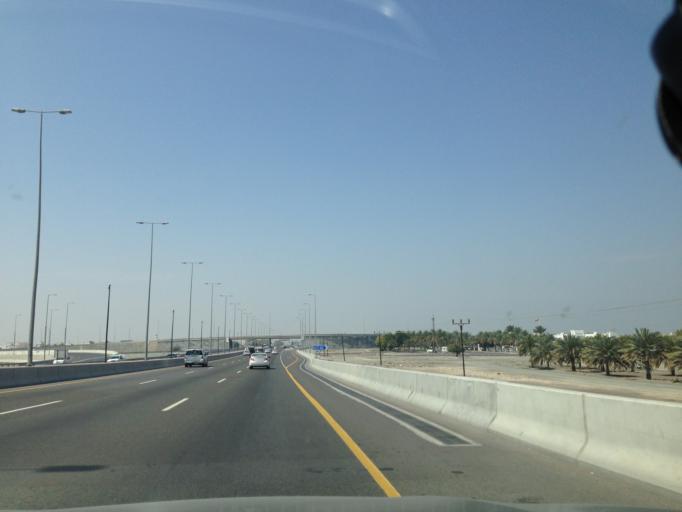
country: OM
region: Muhafazat Masqat
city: As Sib al Jadidah
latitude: 23.6644
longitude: 58.1653
